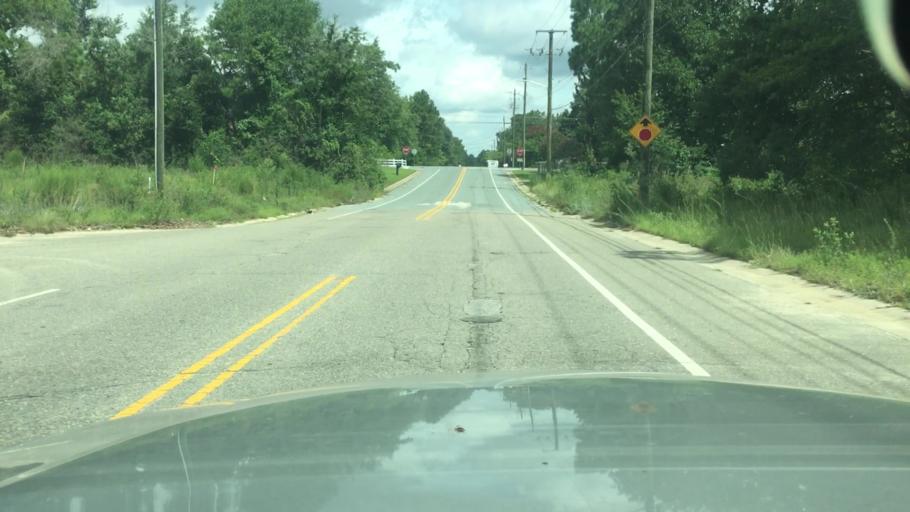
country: US
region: North Carolina
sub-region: Cumberland County
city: Hope Mills
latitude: 35.0204
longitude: -78.9355
